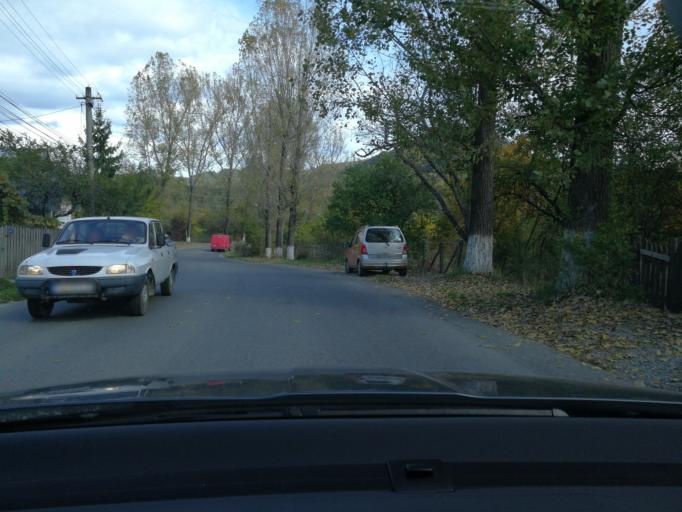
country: RO
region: Prahova
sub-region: Comuna Telega
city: Telega
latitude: 45.1405
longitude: 25.7648
